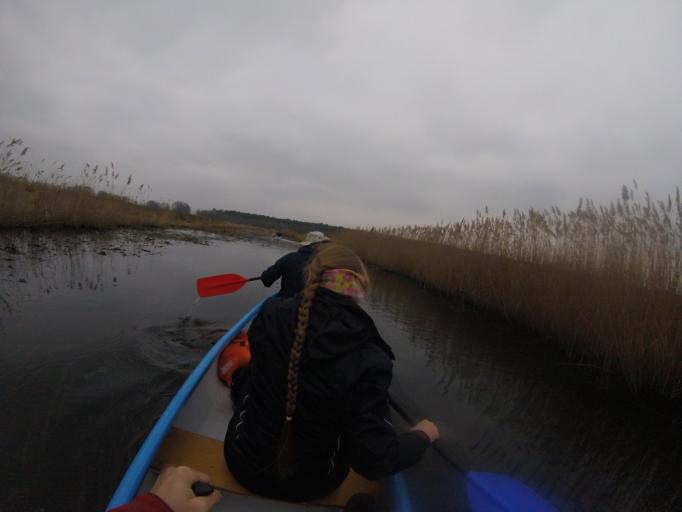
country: HU
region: Zala
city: Heviz
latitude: 46.7644
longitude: 17.2066
